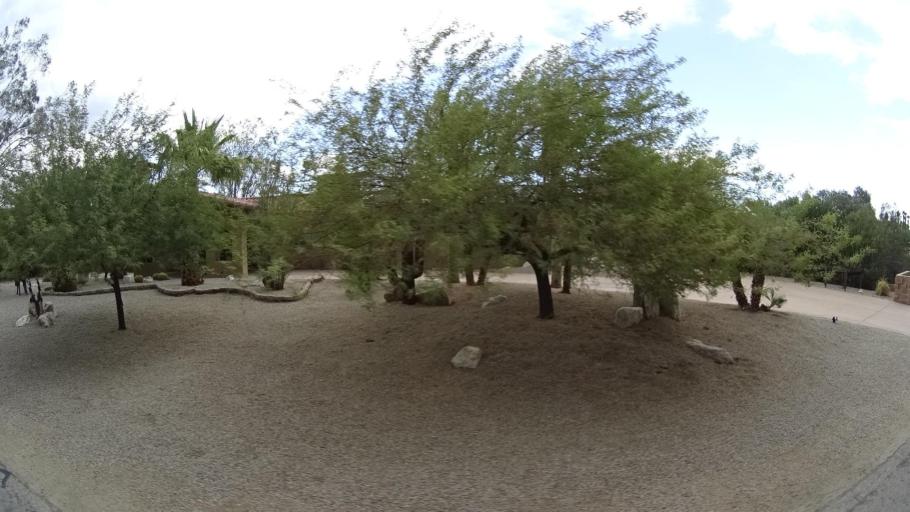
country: US
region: California
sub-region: San Diego County
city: Borrego Springs
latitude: 33.2874
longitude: -116.3982
